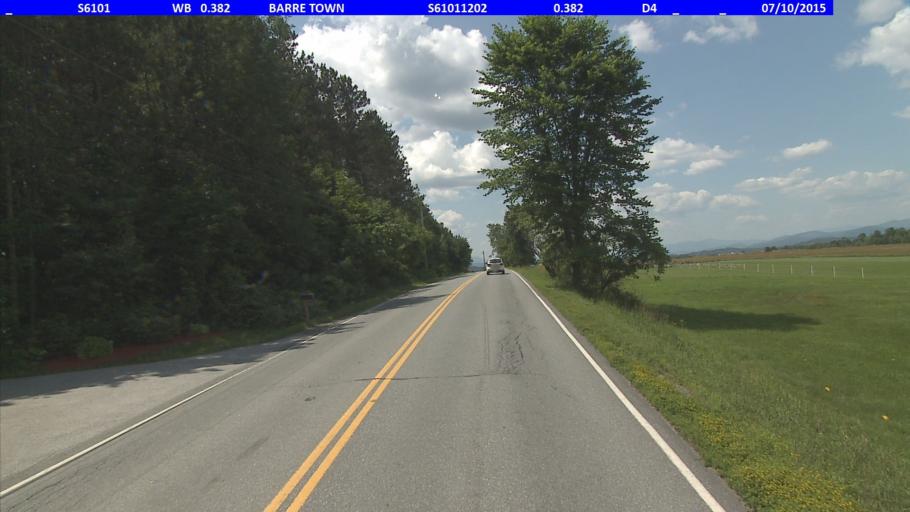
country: US
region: Vermont
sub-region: Washington County
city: South Barre
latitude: 44.1882
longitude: -72.5388
